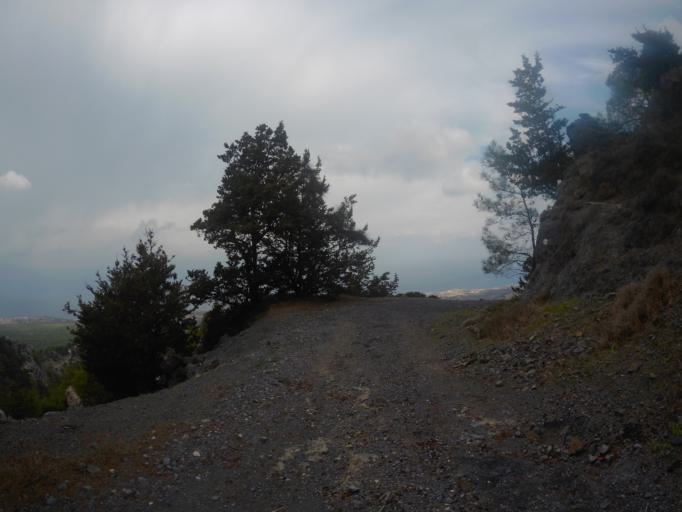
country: CY
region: Ammochostos
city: Lefkonoiko
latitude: 35.3211
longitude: 33.6142
